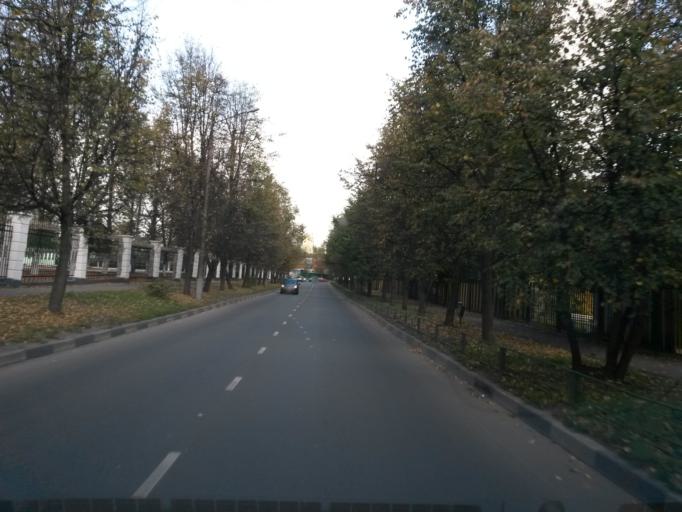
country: RU
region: Moskovskaya
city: Mosrentgen
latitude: 55.6137
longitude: 37.4701
